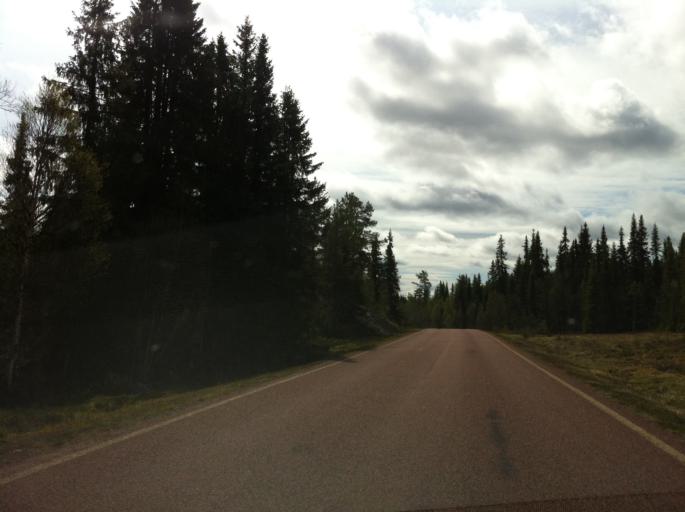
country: NO
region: Hedmark
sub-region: Engerdal
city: Engerdal
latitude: 62.1597
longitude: 12.9454
